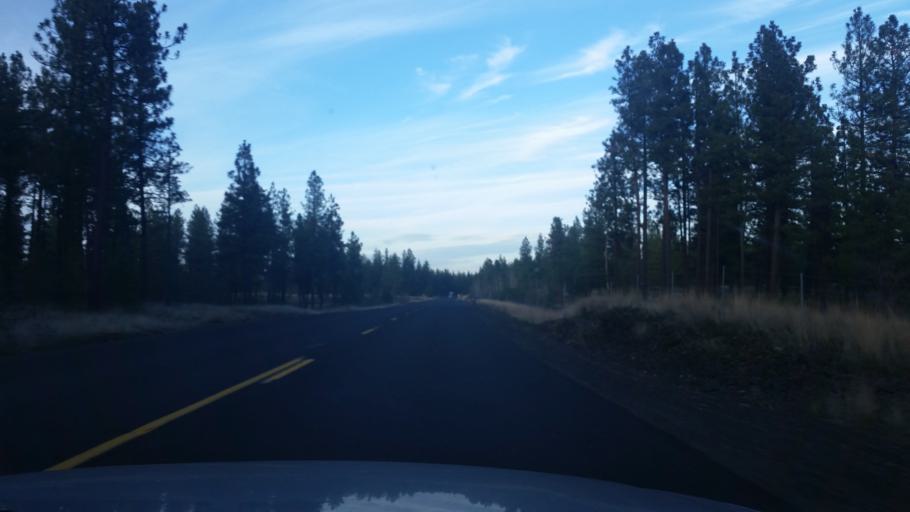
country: US
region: Washington
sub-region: Spokane County
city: Cheney
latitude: 47.4898
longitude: -117.4945
